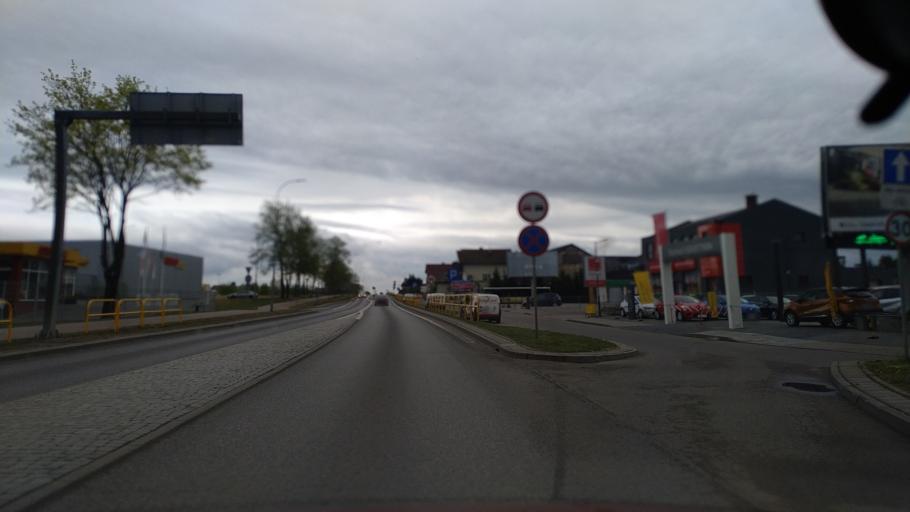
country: PL
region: Pomeranian Voivodeship
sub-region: Powiat starogardzki
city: Starogard Gdanski
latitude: 53.9590
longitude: 18.4950
